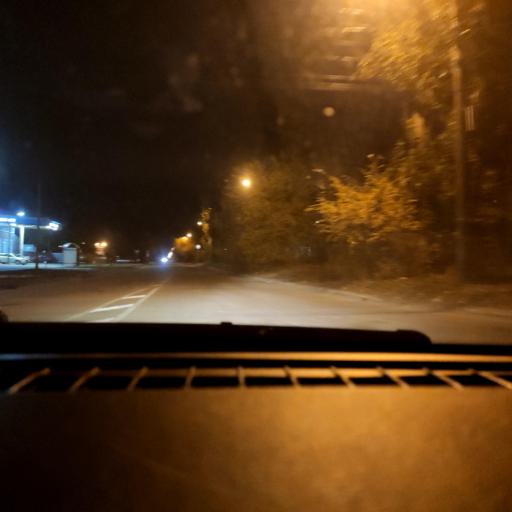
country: RU
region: Voronezj
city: Maslovka
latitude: 51.6007
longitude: 39.2532
